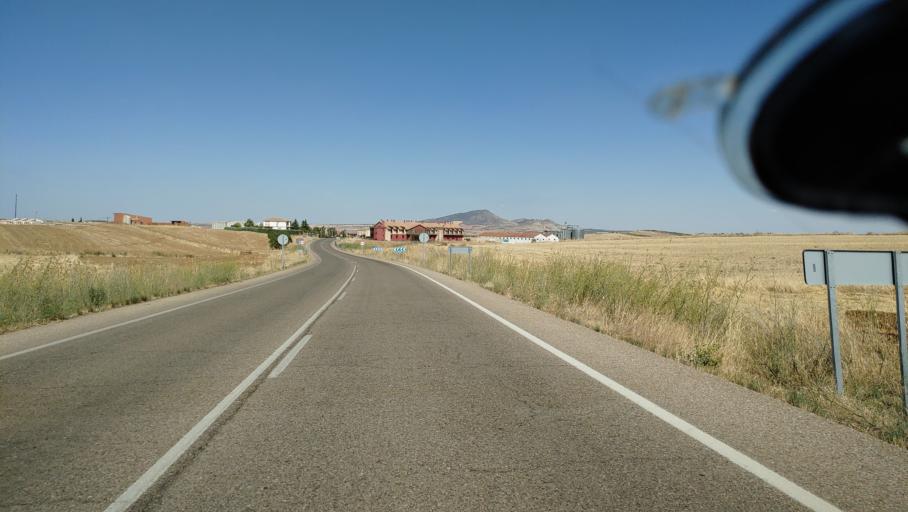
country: ES
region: Castille-La Mancha
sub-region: Province of Toledo
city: Pulgar
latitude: 39.6869
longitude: -4.1630
